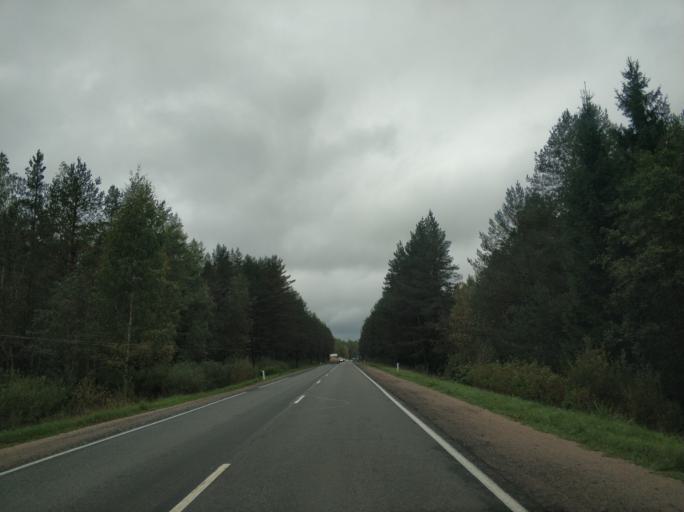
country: RU
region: Leningrad
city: Borisova Griva
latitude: 60.0870
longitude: 30.8758
